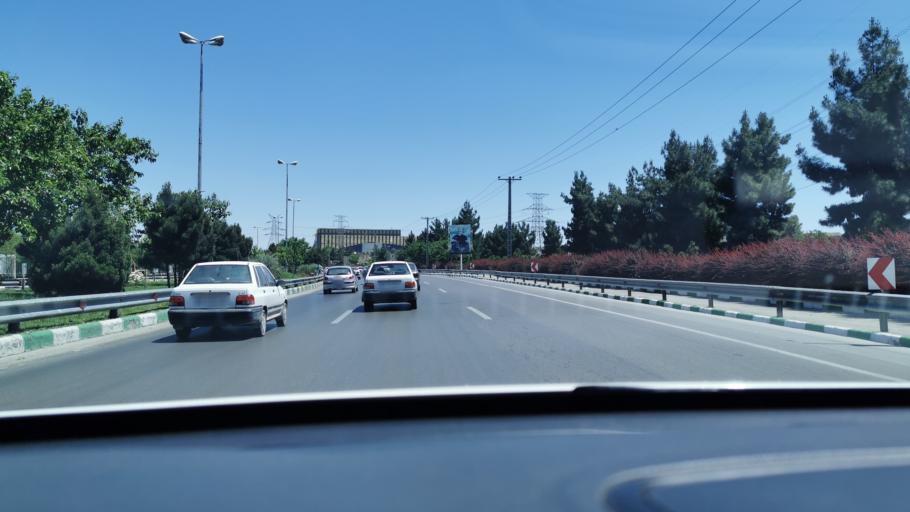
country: IR
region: Razavi Khorasan
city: Mashhad
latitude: 36.2587
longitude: 59.5877
